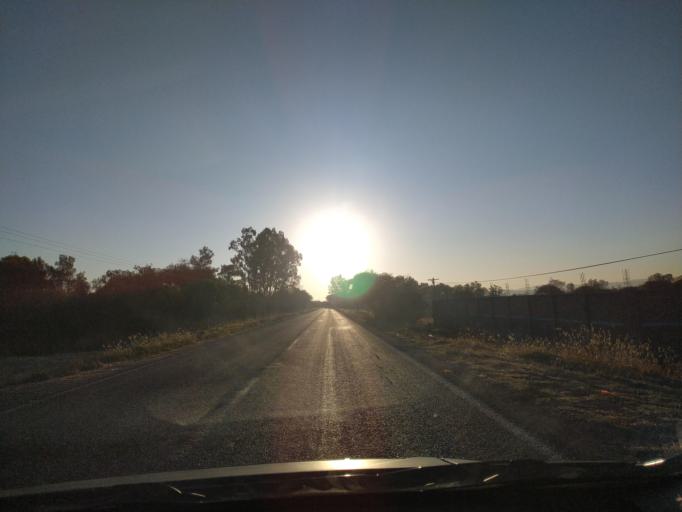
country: MX
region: Guanajuato
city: Ciudad Manuel Doblado
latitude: 20.7407
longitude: -101.9144
